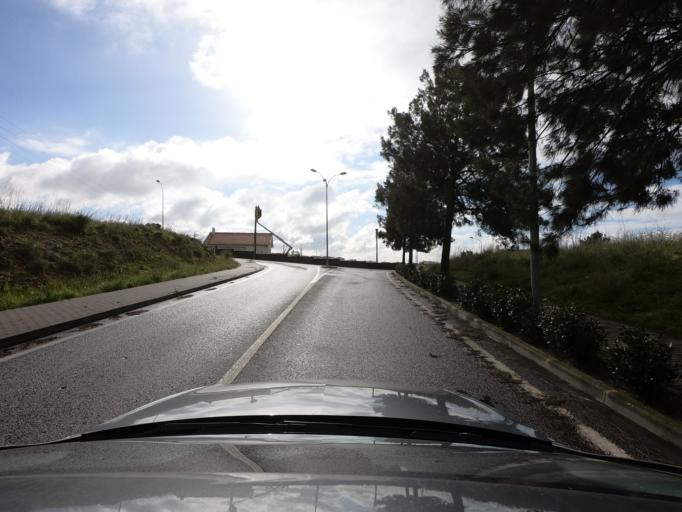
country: PT
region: Lisbon
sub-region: Oeiras
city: Porto Salvo
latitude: 38.7299
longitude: -9.3102
